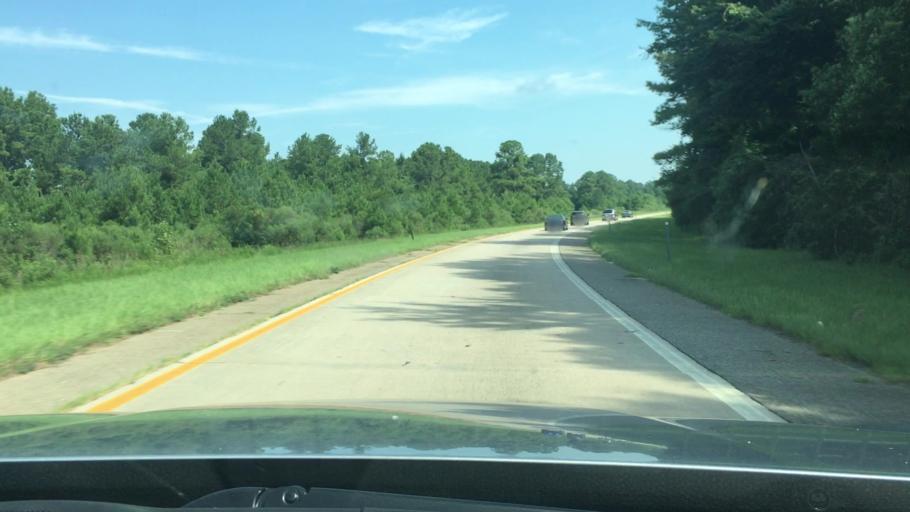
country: US
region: South Carolina
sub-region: Orangeburg County
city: Holly Hill
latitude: 33.3163
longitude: -80.5449
